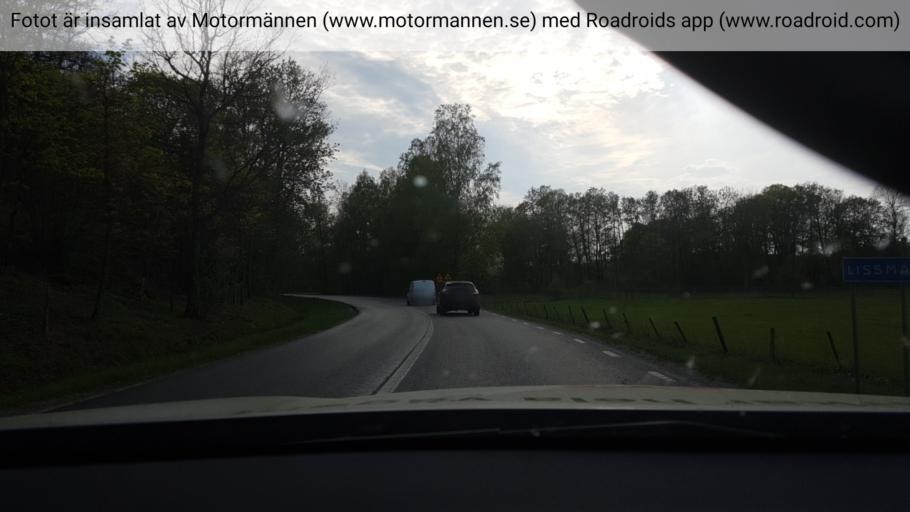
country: SE
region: Stockholm
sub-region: Haninge Kommun
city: Jordbro
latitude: 59.1774
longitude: 18.0788
